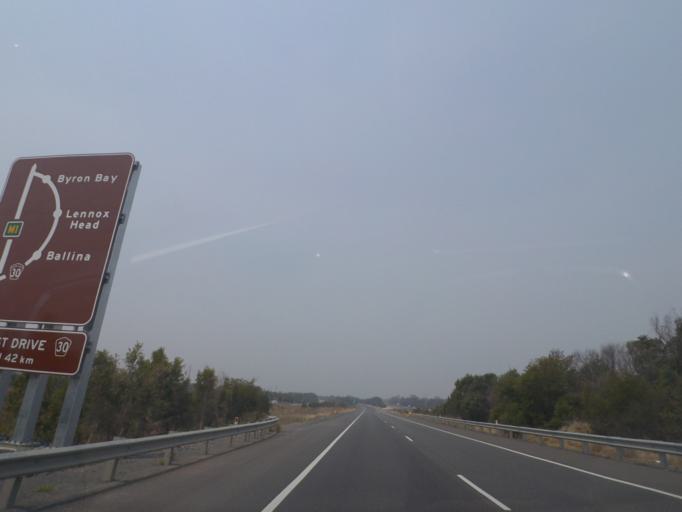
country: AU
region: New South Wales
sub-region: Ballina
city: Ballina
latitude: -28.8654
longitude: 153.5032
